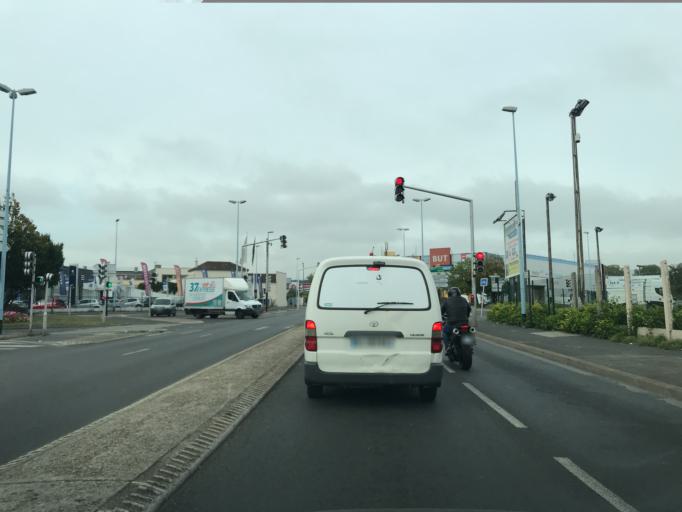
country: FR
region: Ile-de-France
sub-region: Departement de Seine-Saint-Denis
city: Pantin
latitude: 48.9079
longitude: 2.4263
